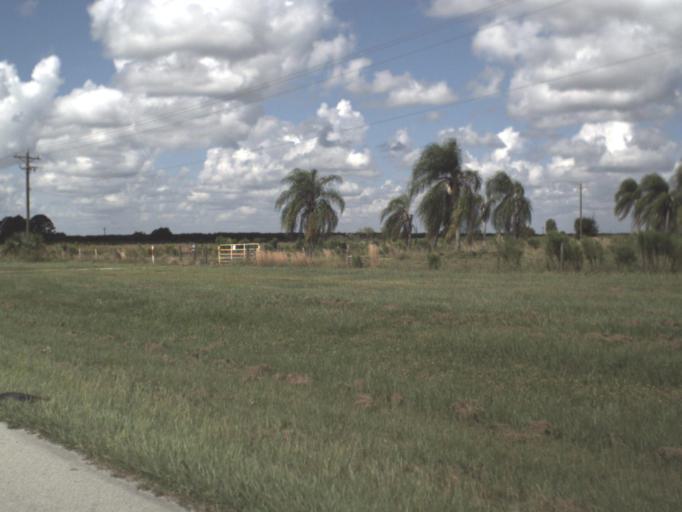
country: US
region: Florida
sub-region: Collier County
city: Immokalee
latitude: 26.4928
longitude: -81.4629
